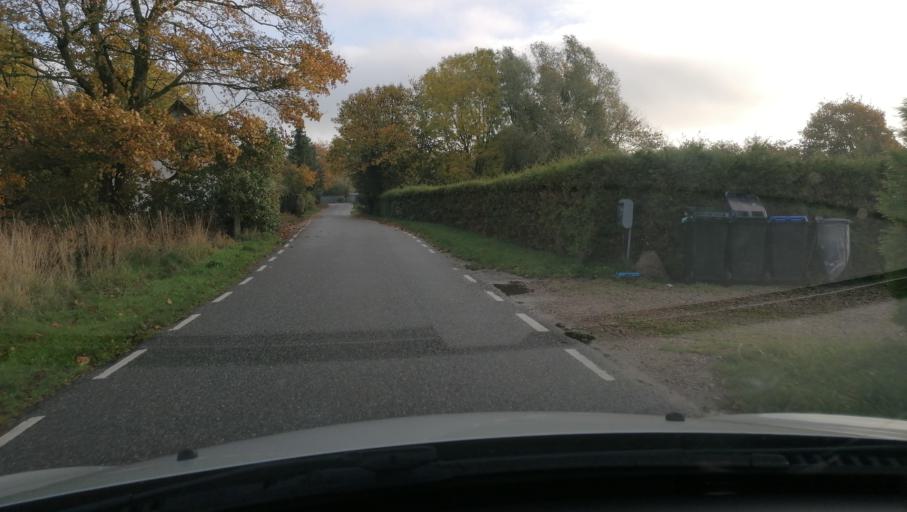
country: DK
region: Zealand
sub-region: Odsherred Kommune
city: Horve
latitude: 55.7439
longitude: 11.4041
